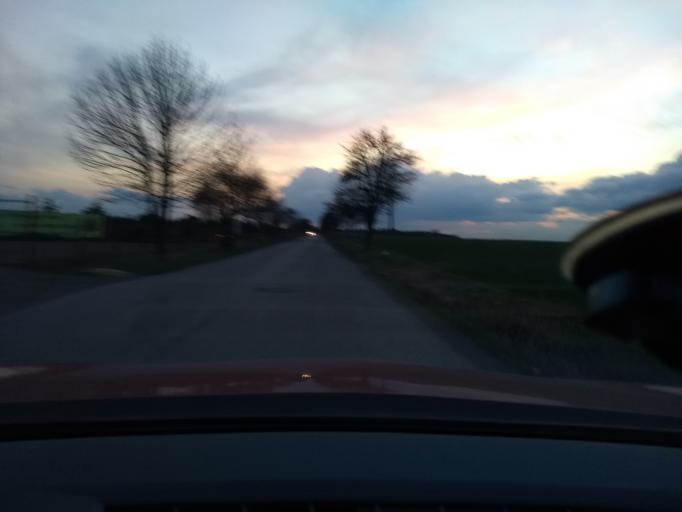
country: CZ
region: Central Bohemia
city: Jenec
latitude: 50.0690
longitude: 14.2222
